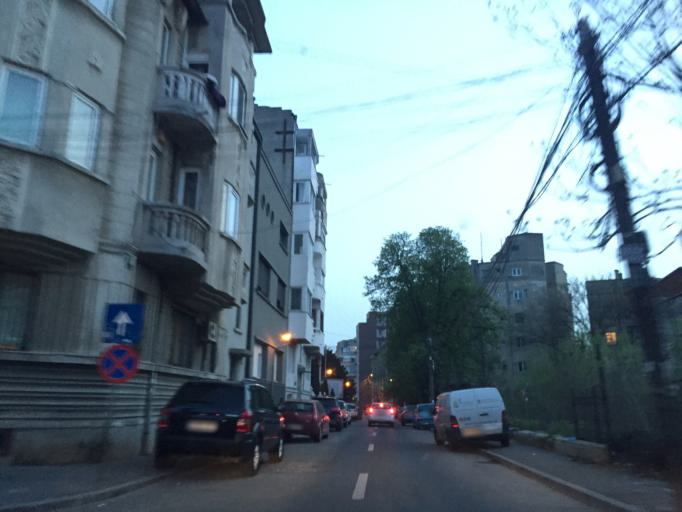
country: RO
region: Bucuresti
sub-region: Municipiul Bucuresti
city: Bucharest
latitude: 44.4350
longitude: 26.1128
